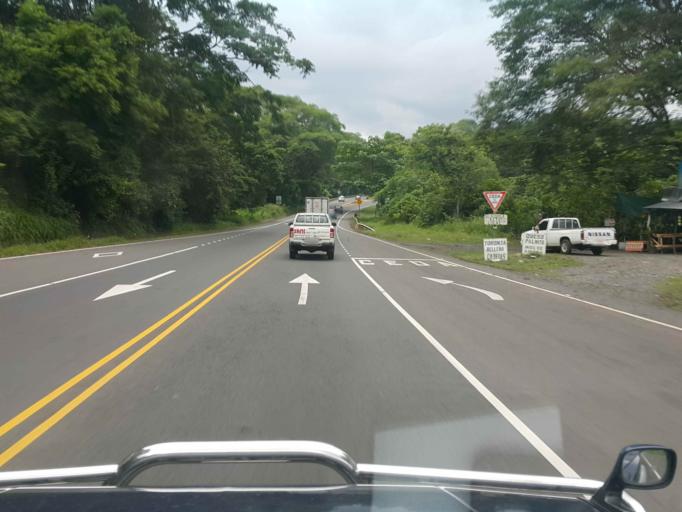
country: CR
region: Alajuela
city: Orotina
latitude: 9.9008
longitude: -84.5462
